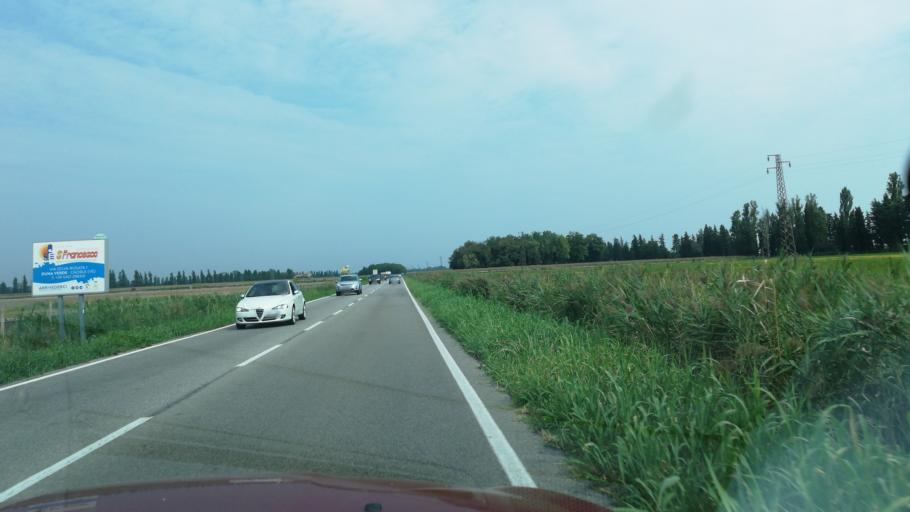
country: IT
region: Veneto
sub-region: Provincia di Venezia
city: La Salute di Livenza
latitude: 45.6105
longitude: 12.8030
